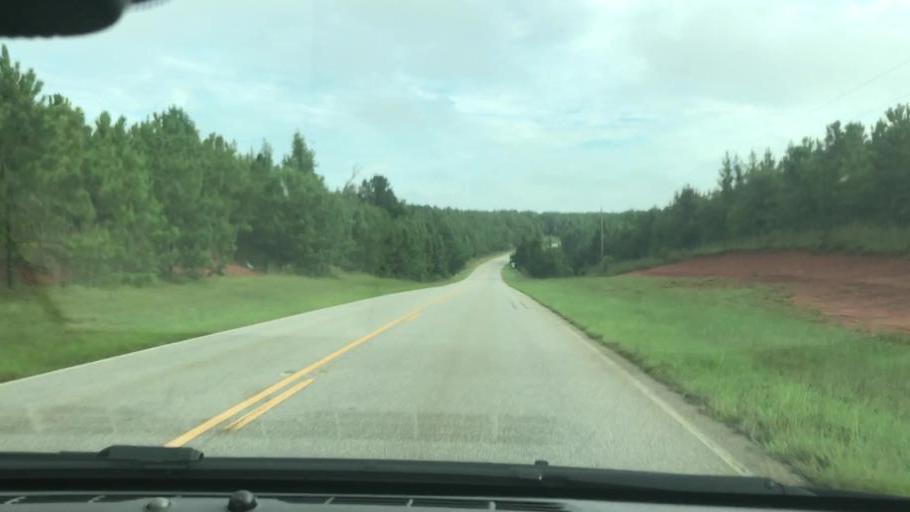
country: US
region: Georgia
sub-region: Stewart County
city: Lumpkin
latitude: 32.0118
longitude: -84.9315
